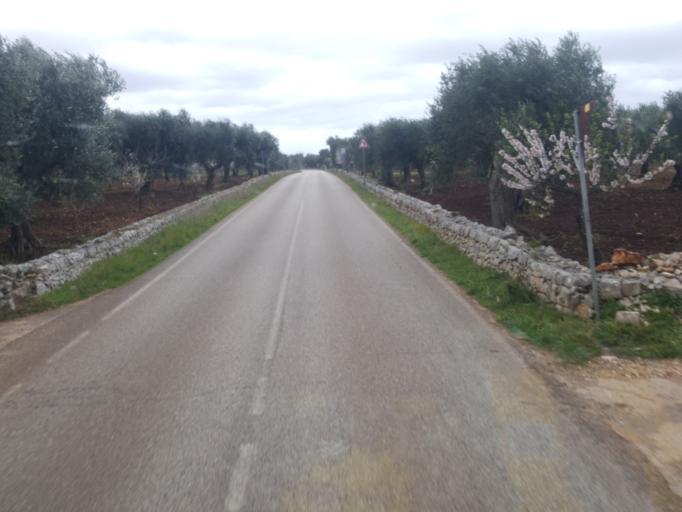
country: IT
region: Apulia
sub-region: Provincia di Bari
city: Conversano
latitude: 40.9436
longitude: 17.0734
